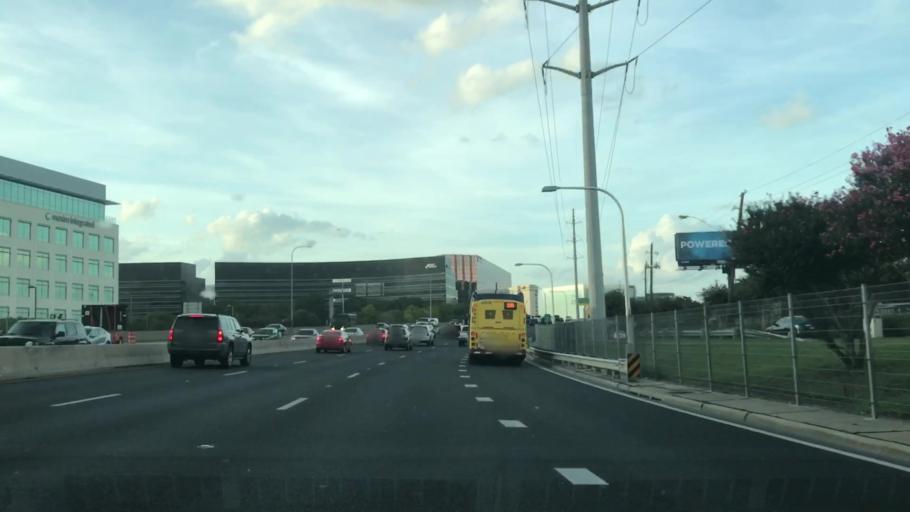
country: US
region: Texas
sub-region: Dallas County
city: Addison
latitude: 32.9454
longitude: -96.8230
